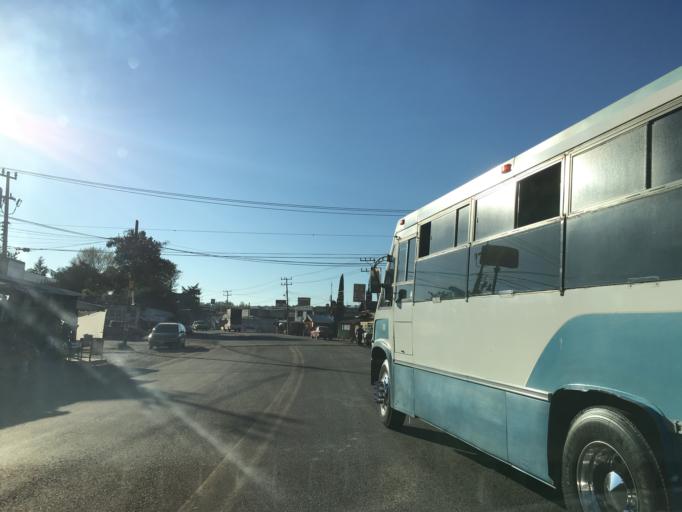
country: MX
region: Michoacan
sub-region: Zitacuaro
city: San Felipe los Alzati (Colonia Nueva)
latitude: 19.4903
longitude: -100.3739
